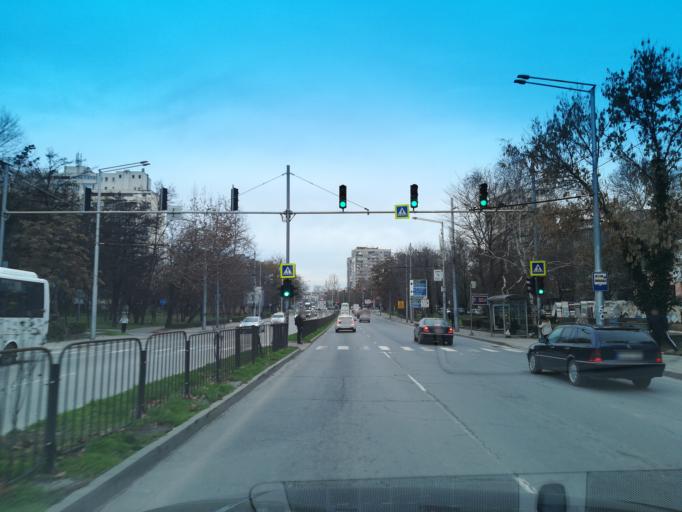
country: BG
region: Plovdiv
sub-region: Obshtina Plovdiv
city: Plovdiv
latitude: 42.1561
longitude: 24.7311
